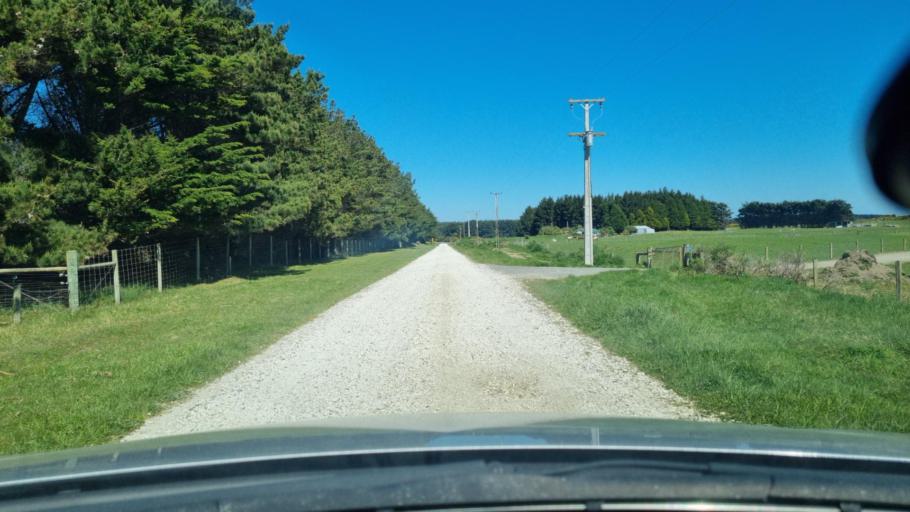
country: NZ
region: Southland
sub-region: Invercargill City
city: Invercargill
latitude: -46.4558
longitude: 168.2740
